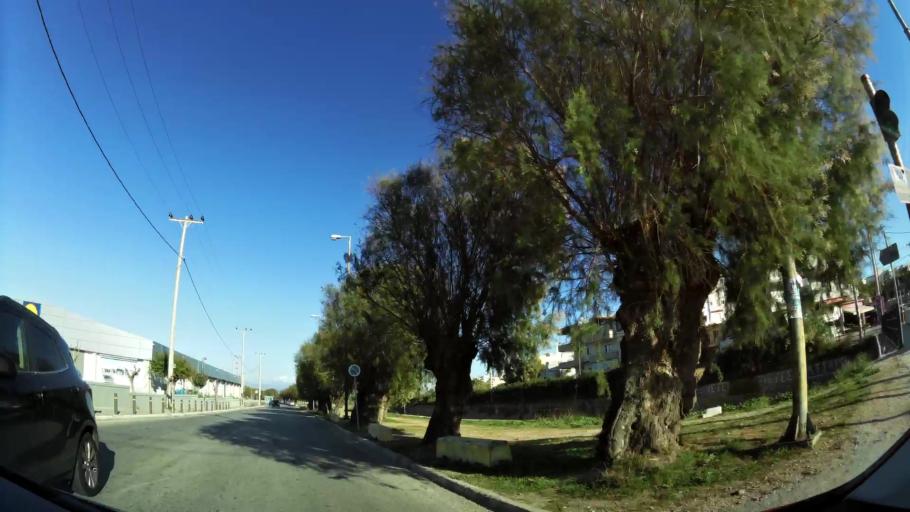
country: GR
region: Attica
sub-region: Nomarchia Anatolikis Attikis
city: Rafina
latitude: 38.0176
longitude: 24.0095
